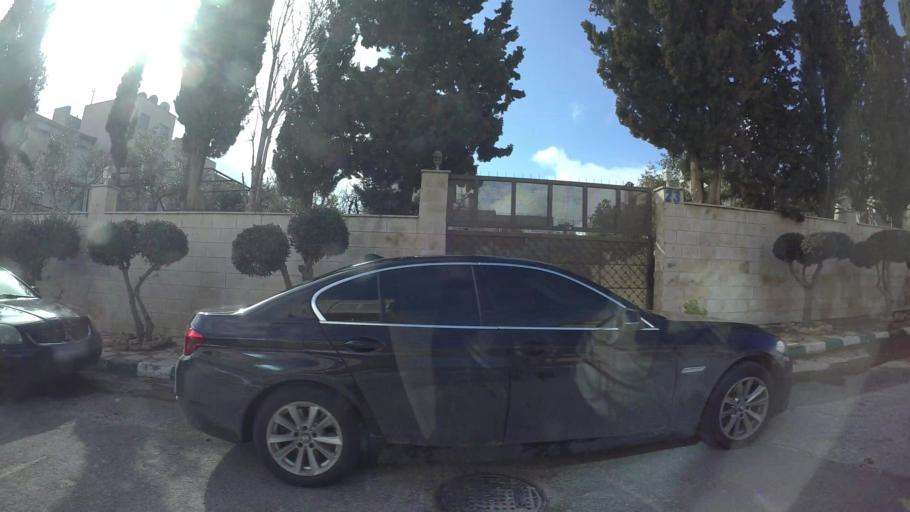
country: JO
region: Amman
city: Al Jubayhah
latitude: 32.0415
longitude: 35.8709
